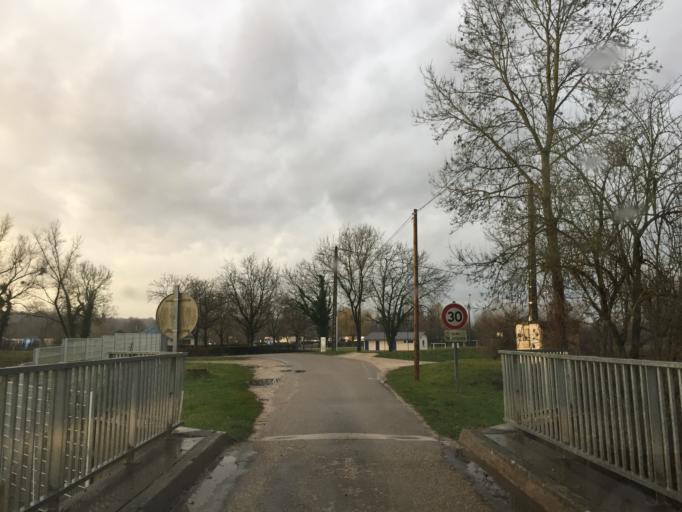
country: FR
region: Franche-Comte
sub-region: Departement du Jura
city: Choisey
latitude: 47.0178
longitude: 5.4825
